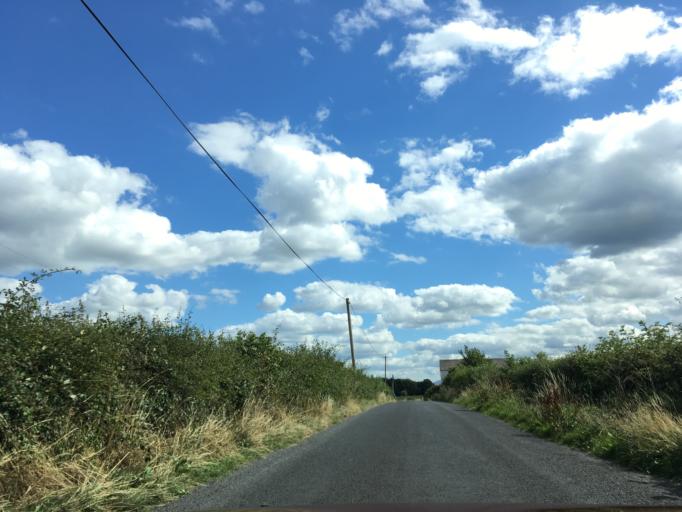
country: IE
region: Munster
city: Cahir
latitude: 52.4620
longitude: -7.9725
